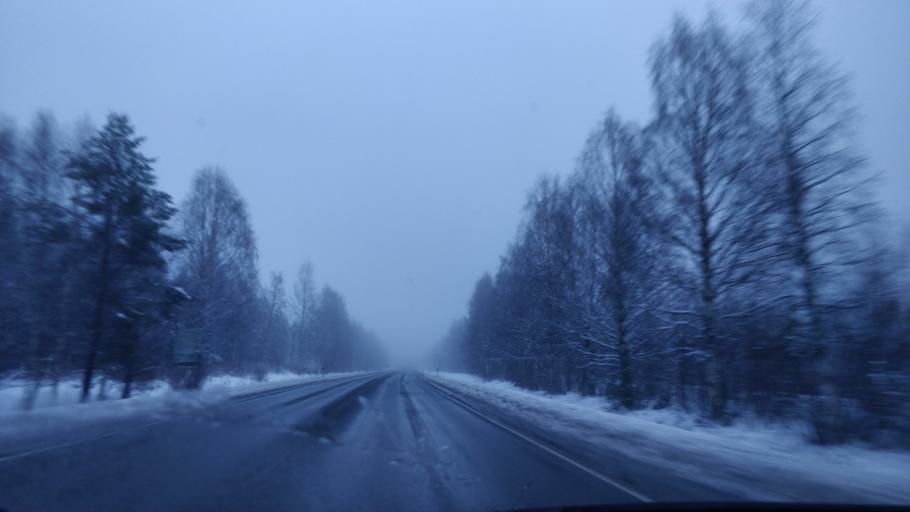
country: FI
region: Lapland
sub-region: Kemi-Tornio
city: Tervola
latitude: 66.1527
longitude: 25.0054
